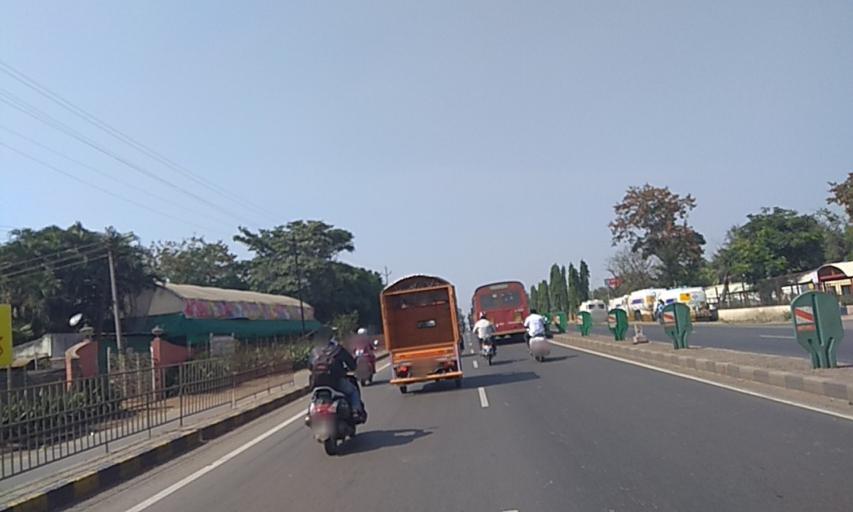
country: IN
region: Maharashtra
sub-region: Pune Division
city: Lohogaon
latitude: 18.4903
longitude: 74.0134
